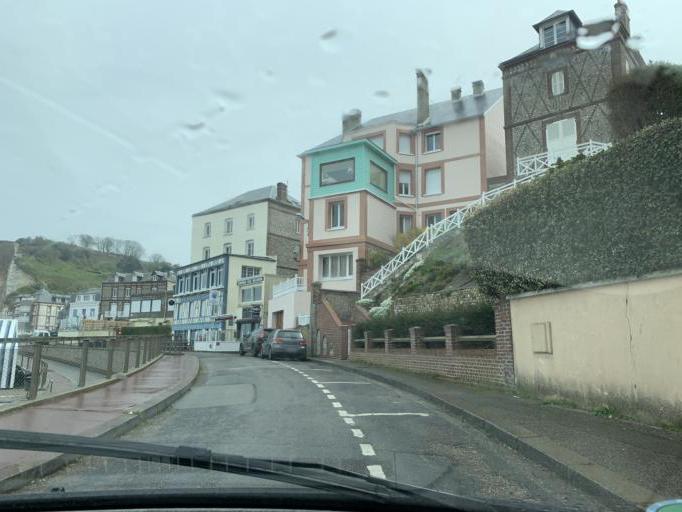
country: FR
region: Haute-Normandie
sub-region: Departement de la Seine-Maritime
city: Yport
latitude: 49.7393
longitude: 0.3089
